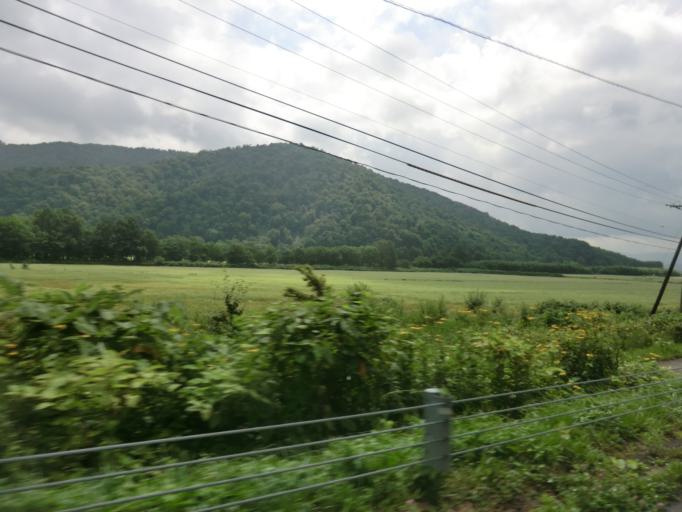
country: JP
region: Hokkaido
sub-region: Asahikawa-shi
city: Asahikawa
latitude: 44.0620
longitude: 142.1406
